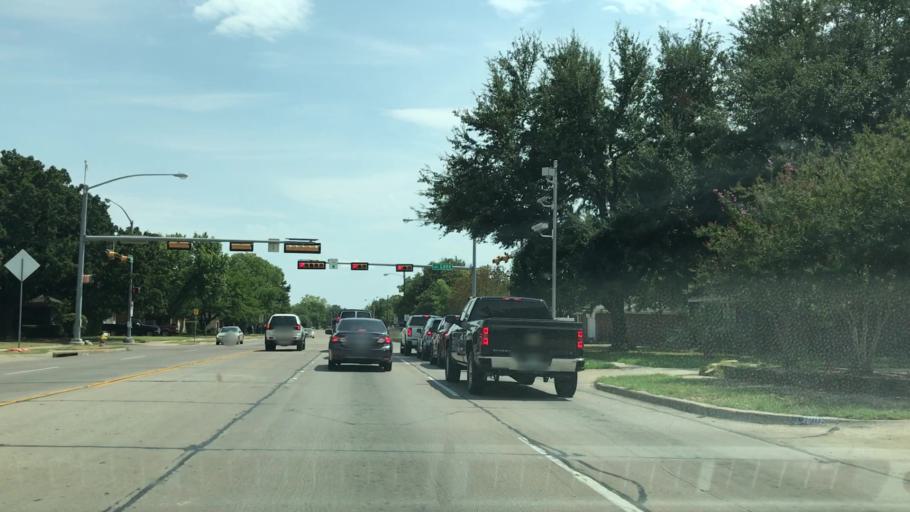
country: US
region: Texas
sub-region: Dallas County
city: Irving
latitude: 32.8339
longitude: -96.9511
